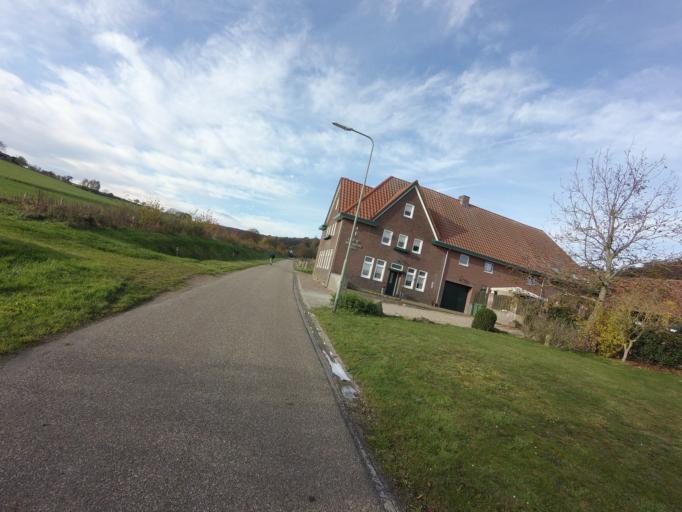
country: BE
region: Wallonia
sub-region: Province de Liege
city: Plombieres
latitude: 50.7887
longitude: 5.9083
